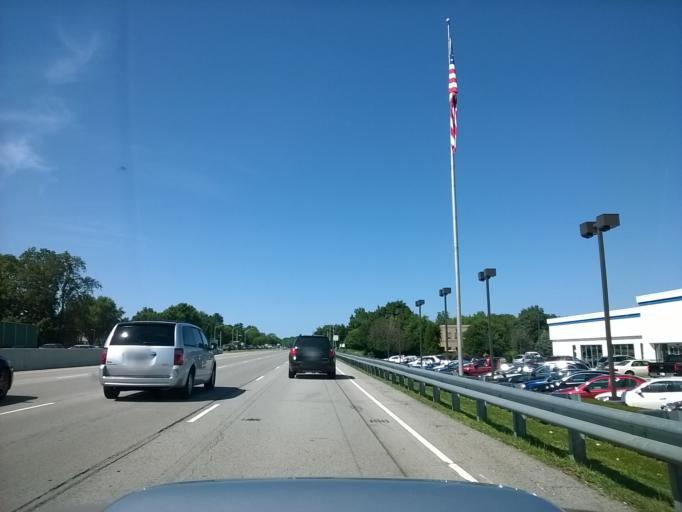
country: US
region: Indiana
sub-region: Hamilton County
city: Carmel
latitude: 39.9282
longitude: -86.1121
